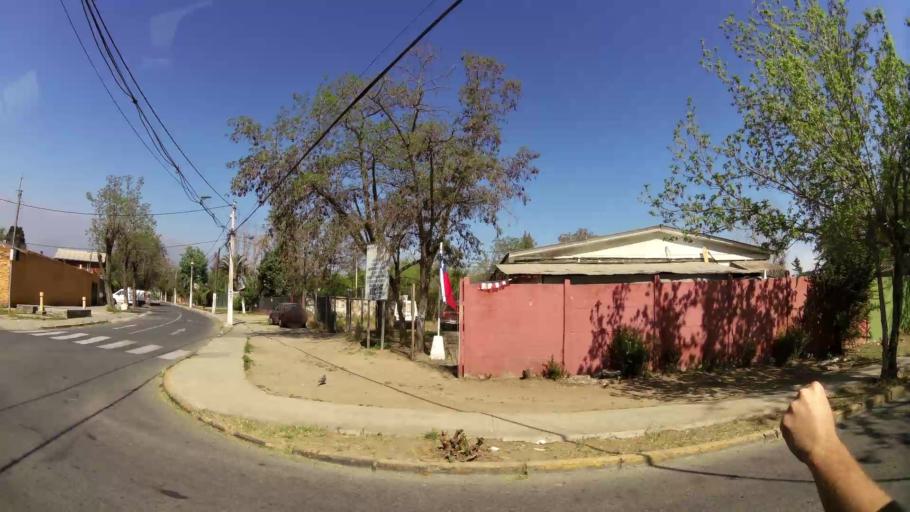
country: CL
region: Santiago Metropolitan
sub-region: Provincia de Santiago
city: Villa Presidente Frei, Nunoa, Santiago, Chile
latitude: -33.4908
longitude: -70.5879
